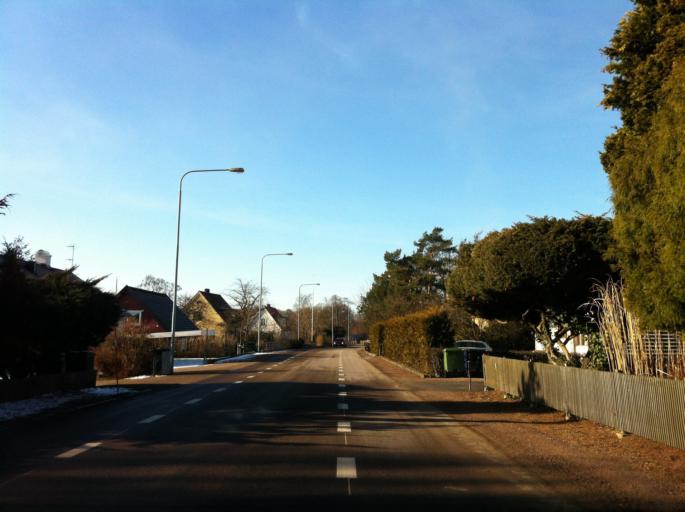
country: SE
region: Skane
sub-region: Helsingborg
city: Hyllinge
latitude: 56.1032
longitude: 12.8047
